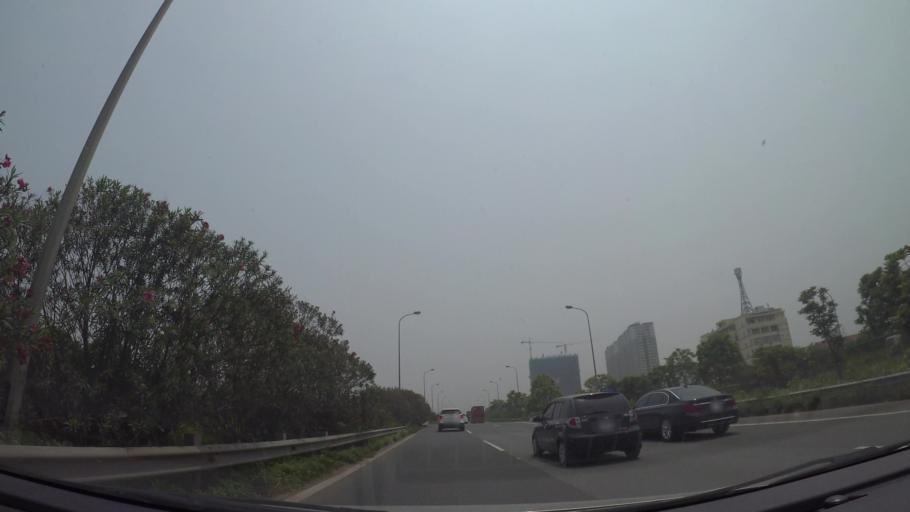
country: VN
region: Ha Noi
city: Cau Dien
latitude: 21.0109
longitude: 105.7166
